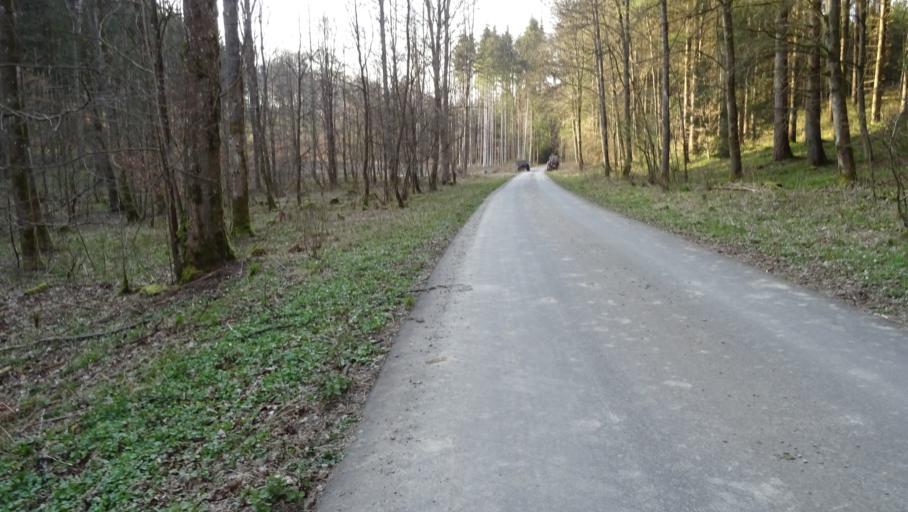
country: DE
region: Baden-Wuerttemberg
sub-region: Regierungsbezirk Stuttgart
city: Roigheim
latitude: 49.3884
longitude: 9.3359
